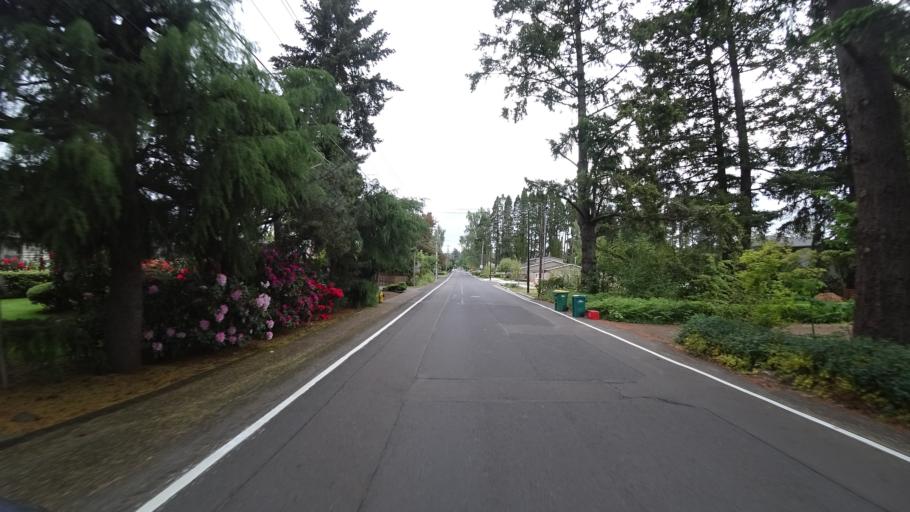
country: US
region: Oregon
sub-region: Washington County
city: Beaverton
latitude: 45.4788
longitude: -122.8172
